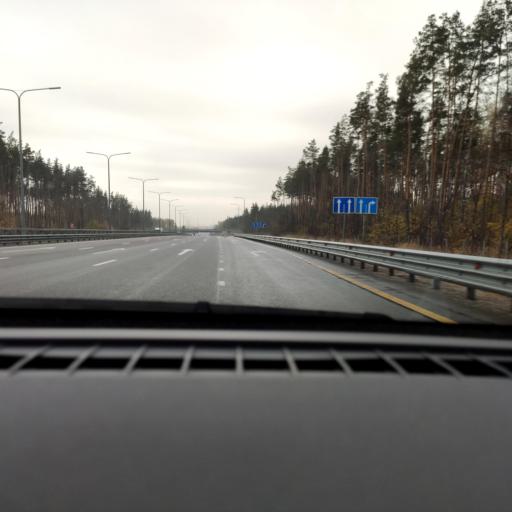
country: RU
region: Voronezj
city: Somovo
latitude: 51.6965
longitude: 39.3033
